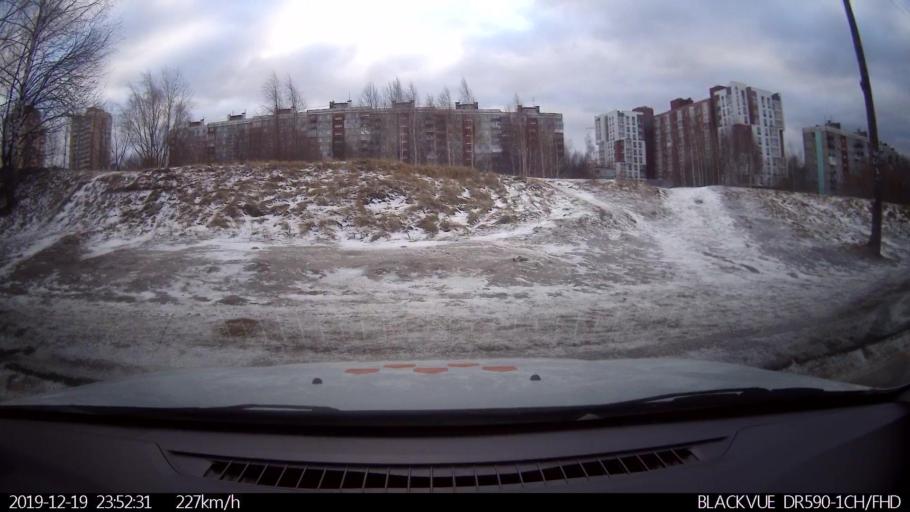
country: RU
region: Vologda
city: Molochnoye
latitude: 58.9848
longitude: 39.4864
